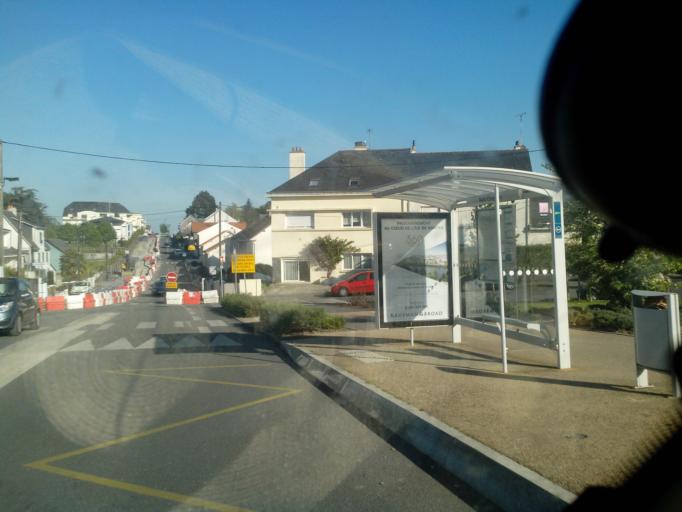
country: FR
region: Pays de la Loire
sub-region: Departement de la Loire-Atlantique
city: Orvault
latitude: 47.2545
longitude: -1.6008
